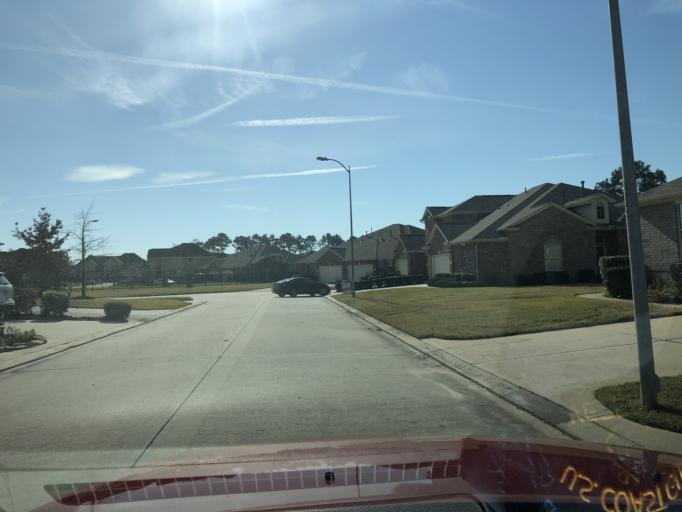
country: US
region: Texas
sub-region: Harris County
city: Tomball
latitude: 30.0381
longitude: -95.5551
